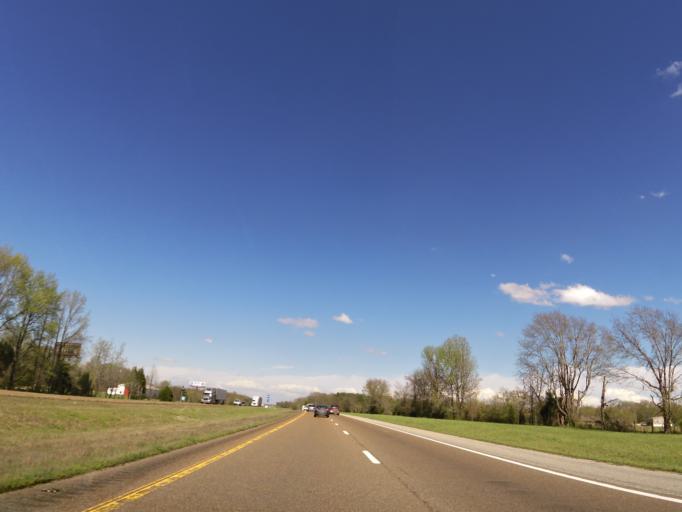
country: US
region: Tennessee
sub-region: Gibson County
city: Medina
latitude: 35.7289
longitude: -88.5994
